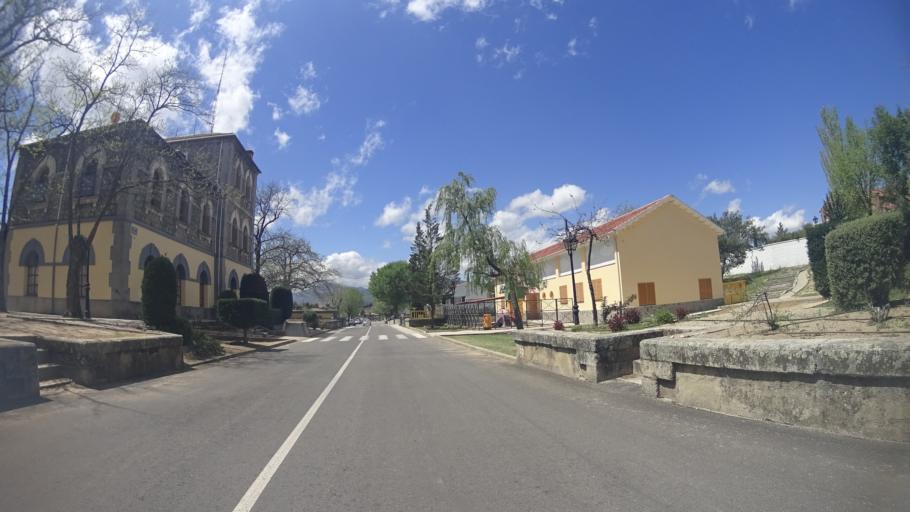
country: ES
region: Madrid
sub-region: Provincia de Madrid
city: San Martin de Valdeiglesias
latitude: 40.3653
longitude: -4.3979
